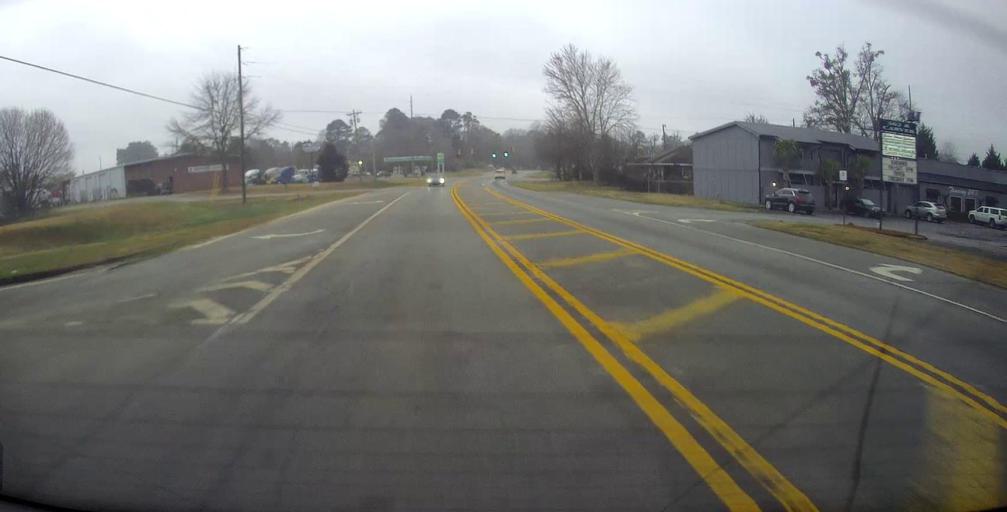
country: US
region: Georgia
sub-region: Spalding County
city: Griffin
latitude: 33.2264
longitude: -84.2965
